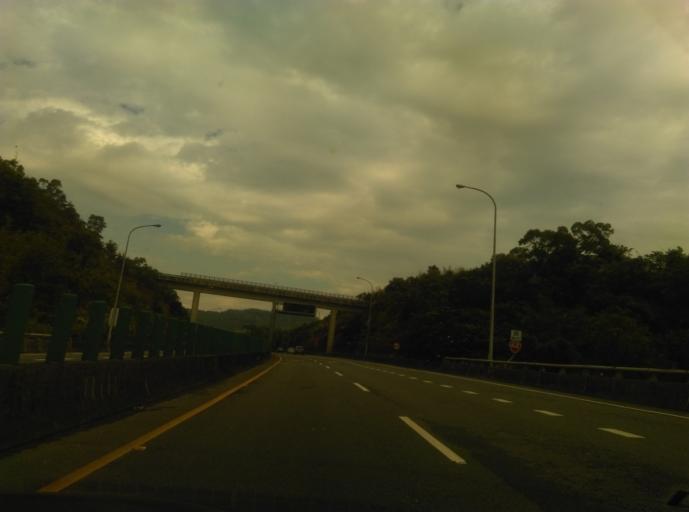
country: TW
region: Taiwan
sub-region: Keelung
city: Keelung
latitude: 25.1171
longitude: 121.6955
